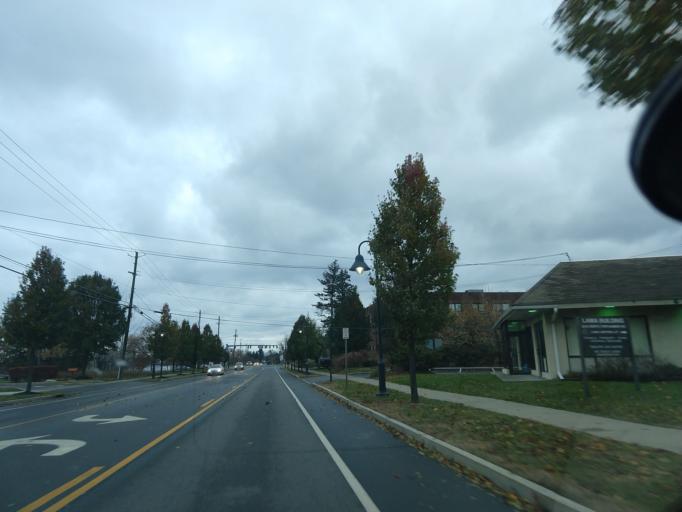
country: US
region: New York
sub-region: Tompkins County
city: Lansing
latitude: 42.4849
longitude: -76.4864
